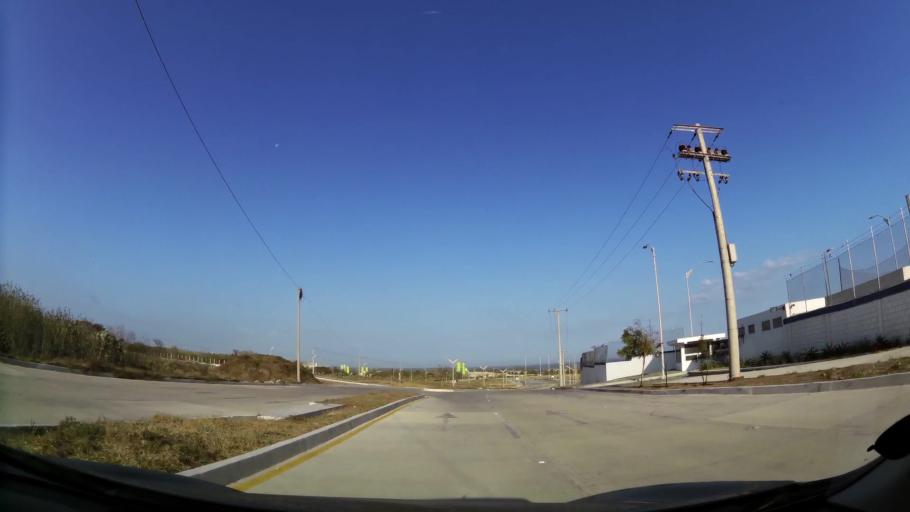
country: CO
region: Atlantico
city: Barranquilla
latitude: 11.0309
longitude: -74.8278
